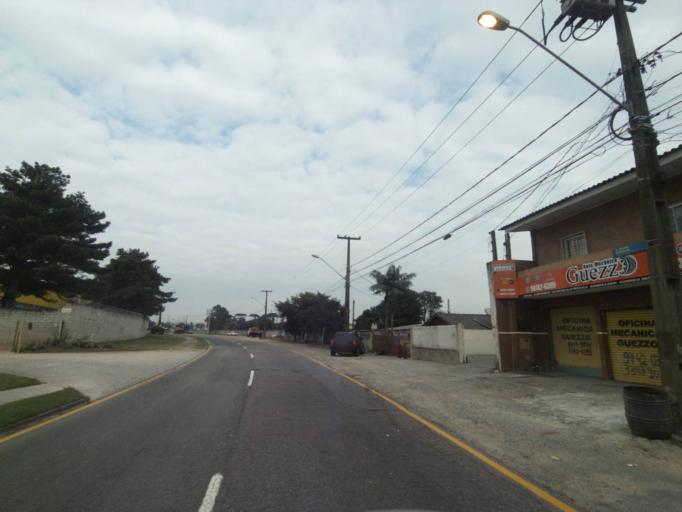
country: BR
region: Parana
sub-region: Curitiba
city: Curitiba
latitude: -25.5175
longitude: -49.3267
